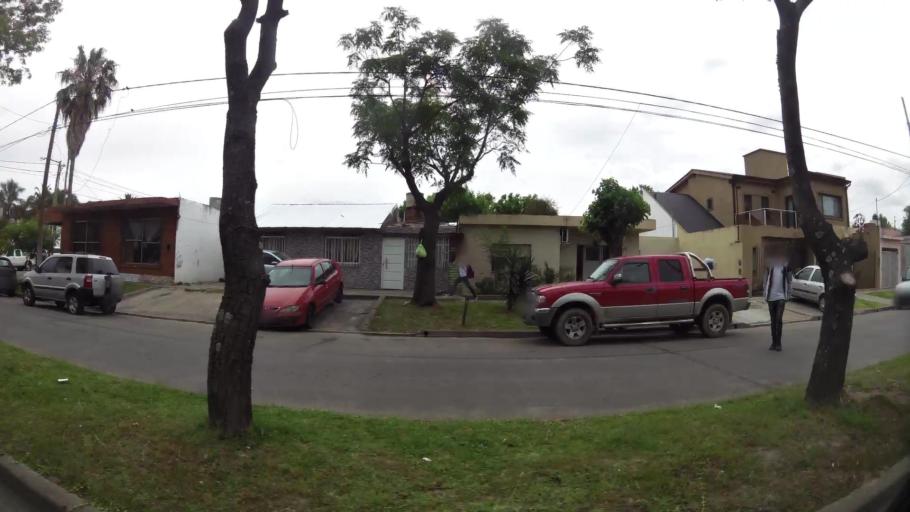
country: AR
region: Buenos Aires
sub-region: Partido de Campana
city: Campana
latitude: -34.1761
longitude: -58.9528
